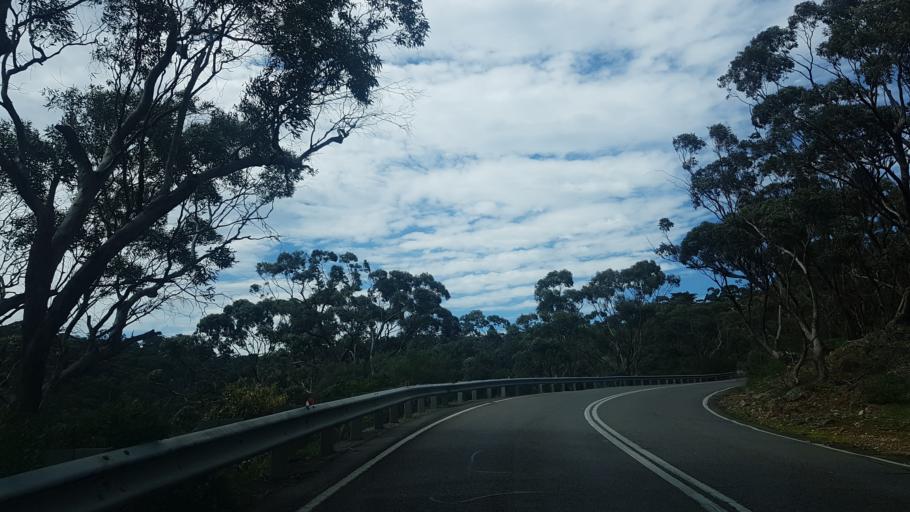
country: AU
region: South Australia
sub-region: Mitcham
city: Belair
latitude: -35.0006
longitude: 138.6092
